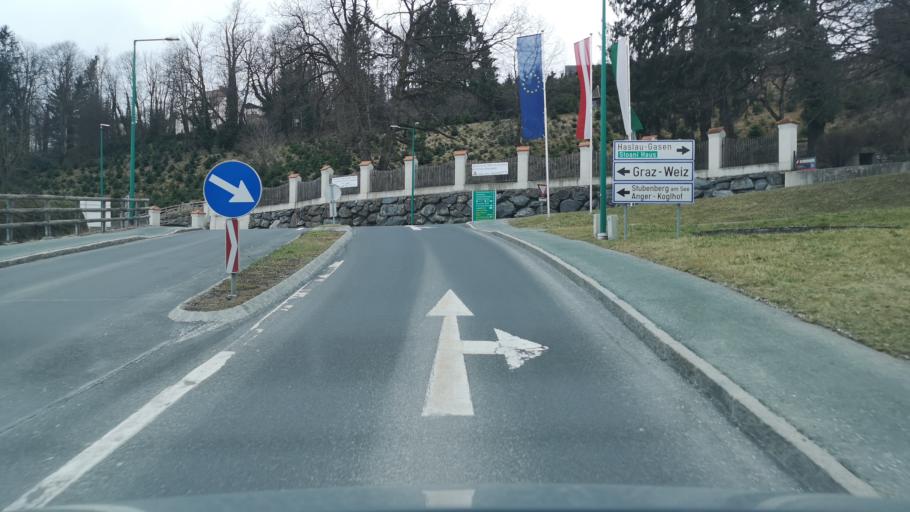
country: AT
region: Styria
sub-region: Politischer Bezirk Weiz
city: Birkfeld
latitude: 47.3535
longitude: 15.6951
